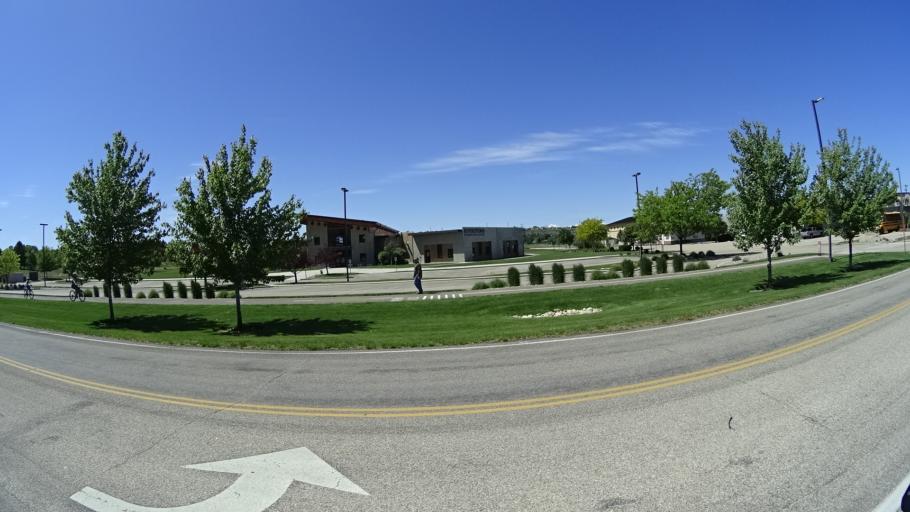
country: US
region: Idaho
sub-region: Ada County
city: Boise
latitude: 43.5654
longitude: -116.1143
